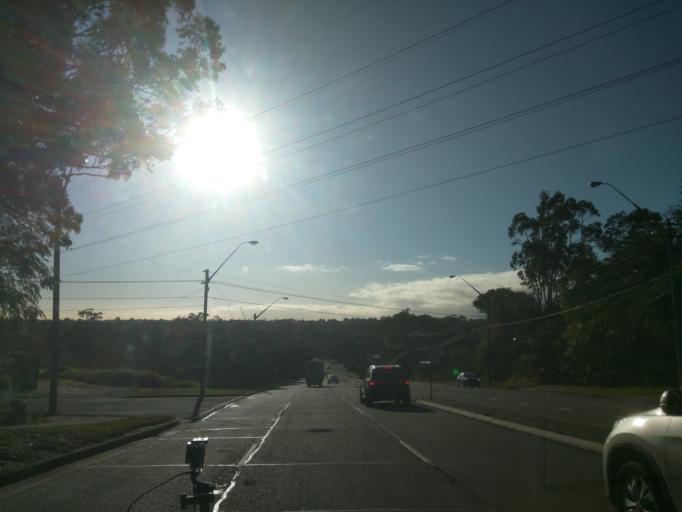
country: AU
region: New South Wales
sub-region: Bankstown
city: Padstow
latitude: -33.9657
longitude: 151.0372
